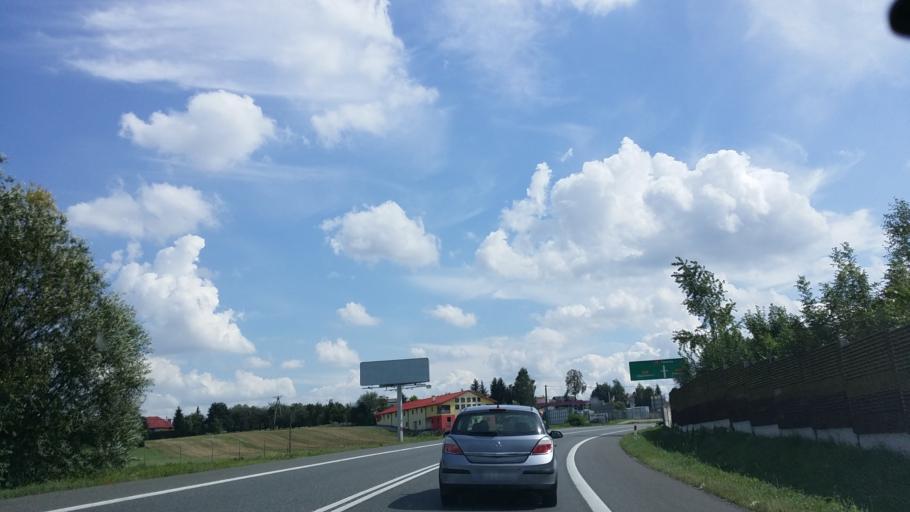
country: PL
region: Lesser Poland Voivodeship
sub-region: Powiat wielicki
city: Wieliczka
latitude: 49.9929
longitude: 20.0795
